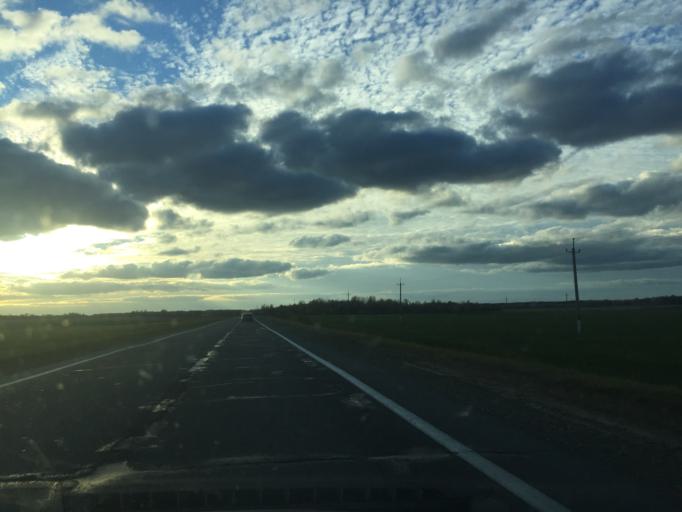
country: BY
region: Vitebsk
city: Myory
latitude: 55.8204
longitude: 27.7100
